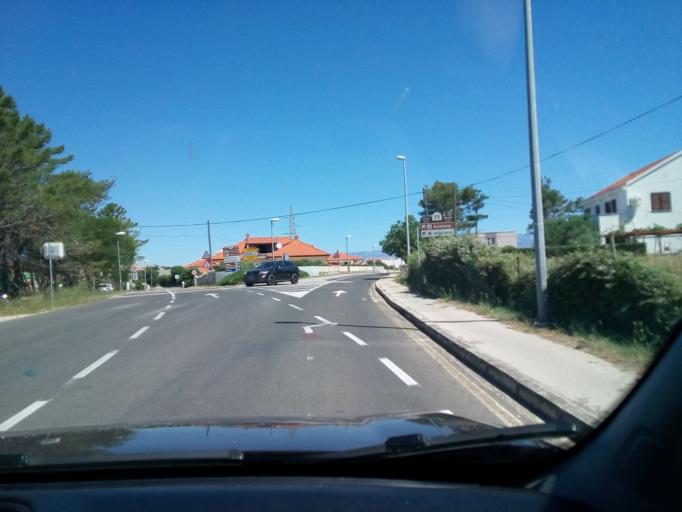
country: HR
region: Zadarska
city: Nin
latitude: 44.2367
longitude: 15.1816
